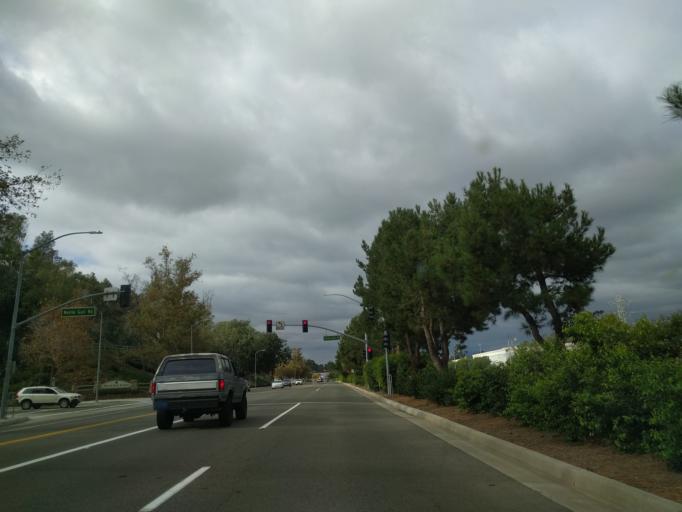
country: US
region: California
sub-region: Orange County
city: Mission Viejo
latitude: 33.5874
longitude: -117.6741
